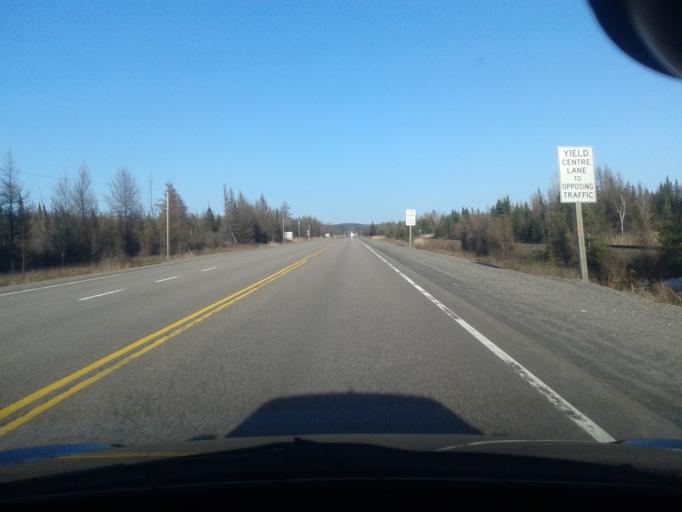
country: CA
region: Ontario
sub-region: Nipissing District
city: North Bay
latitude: 46.3696
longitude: -79.7349
